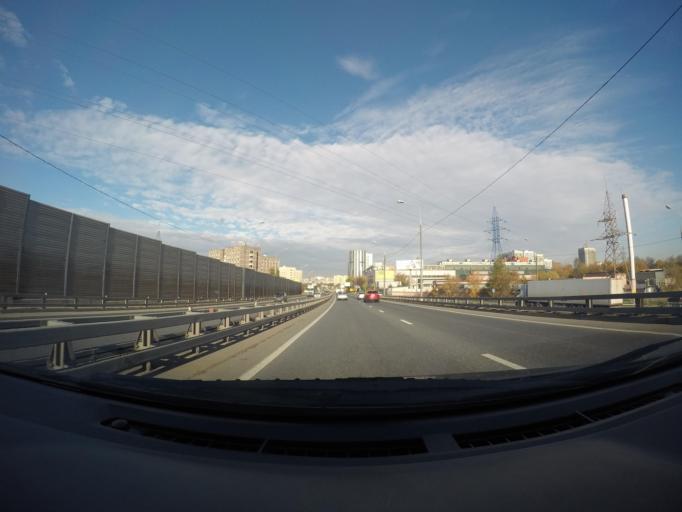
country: RU
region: Moskovskaya
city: Druzhba
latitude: 55.9114
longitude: 37.7763
